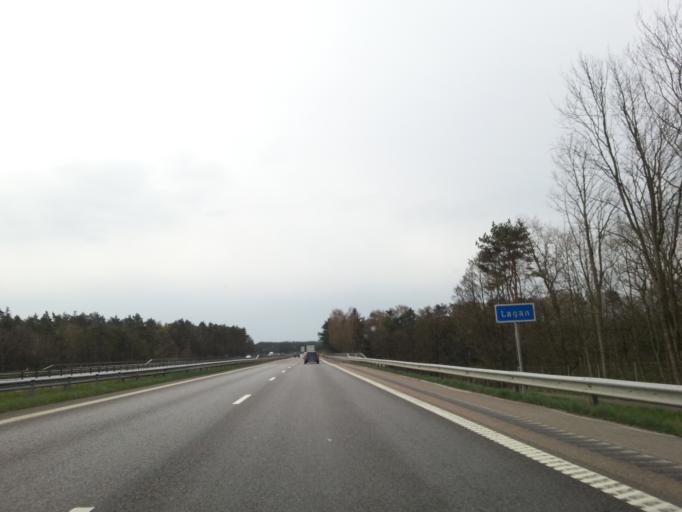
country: SE
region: Halland
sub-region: Laholms Kommun
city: Mellbystrand
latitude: 56.5337
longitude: 12.9676
